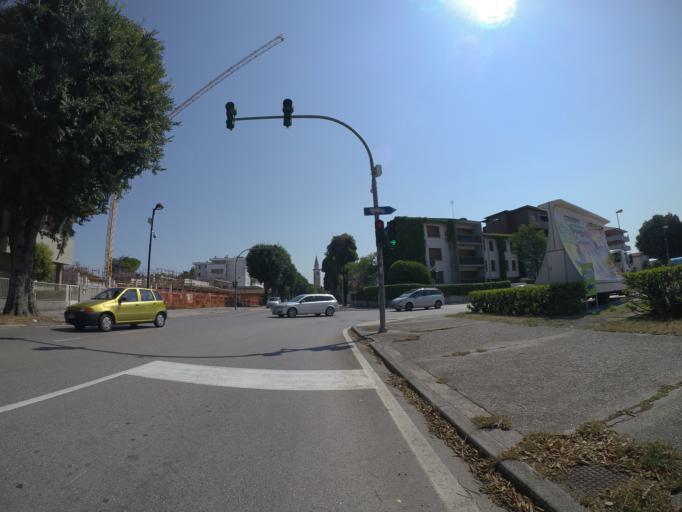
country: IT
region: Friuli Venezia Giulia
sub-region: Provincia di Udine
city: Codroipo
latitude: 45.9623
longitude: 12.9721
